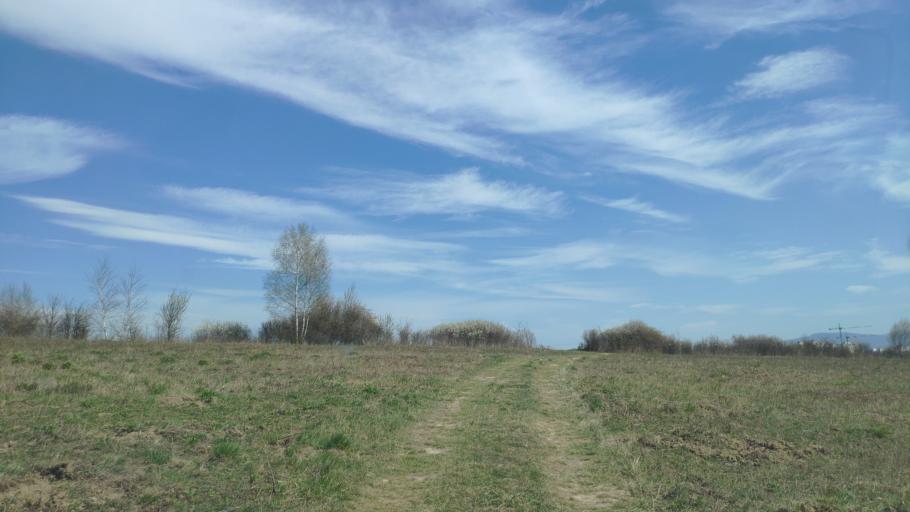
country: SK
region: Kosicky
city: Kosice
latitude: 48.7235
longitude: 21.1952
